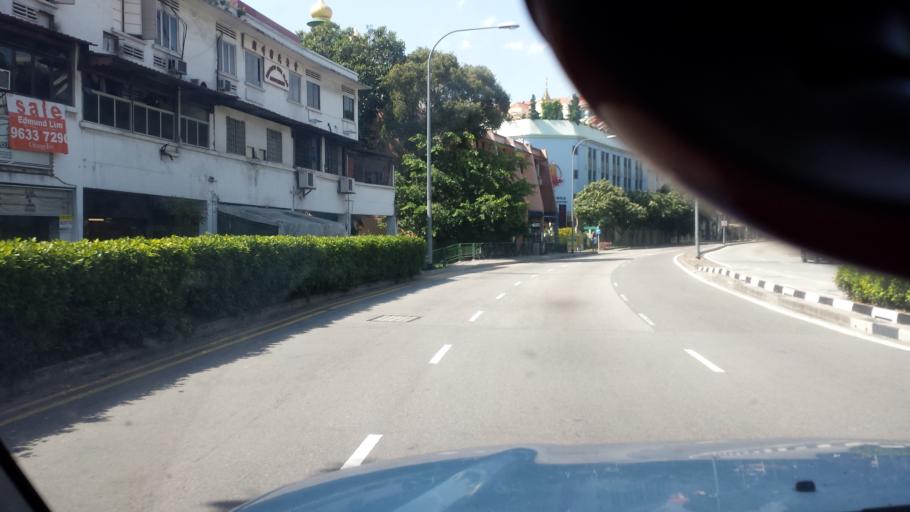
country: SG
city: Singapore
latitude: 1.3090
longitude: 103.8778
